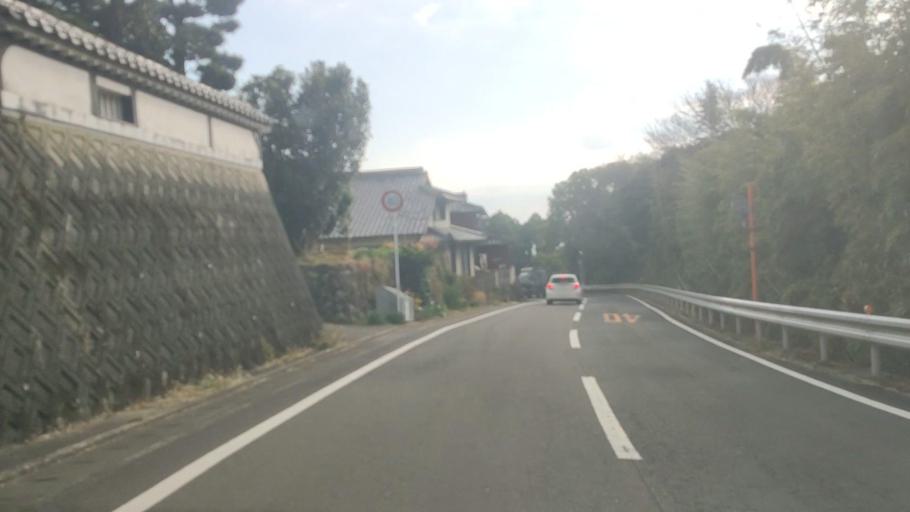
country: JP
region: Nagasaki
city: Shimabara
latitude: 32.6742
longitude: 130.2818
